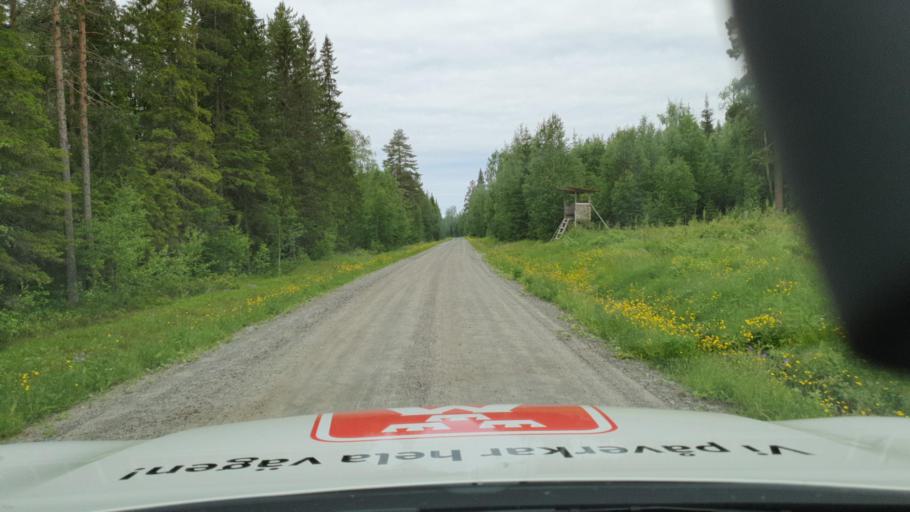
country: SE
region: Vaesterbotten
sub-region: Skelleftea Kommun
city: Burtraesk
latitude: 64.4436
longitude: 20.3591
